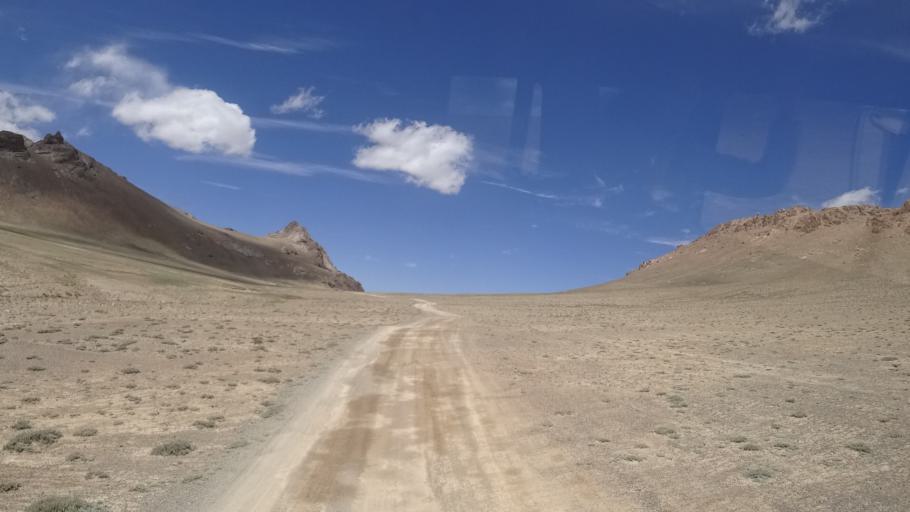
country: TJ
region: Gorno-Badakhshan
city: Murghob
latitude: 37.8409
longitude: 74.1679
